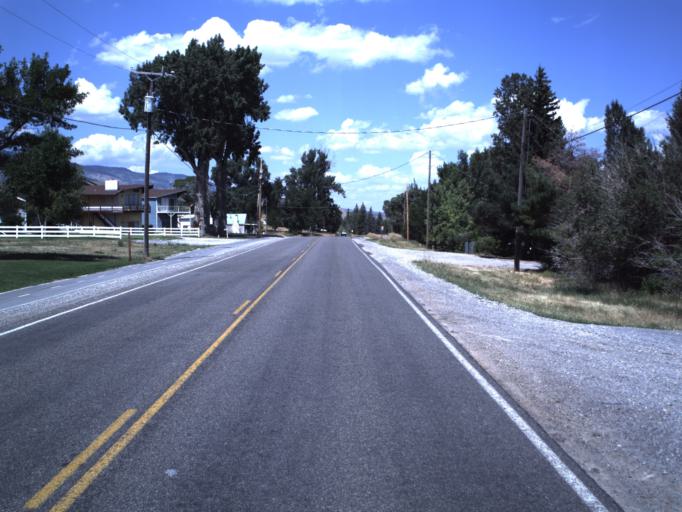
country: US
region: Idaho
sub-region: Bear Lake County
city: Paris
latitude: 41.9158
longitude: -111.3923
